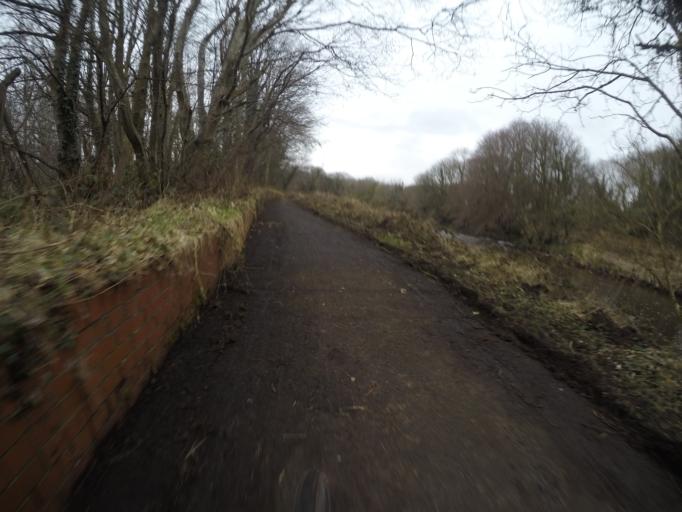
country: GB
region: Scotland
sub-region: North Ayrshire
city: Kilwinning
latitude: 55.6423
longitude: -4.6866
